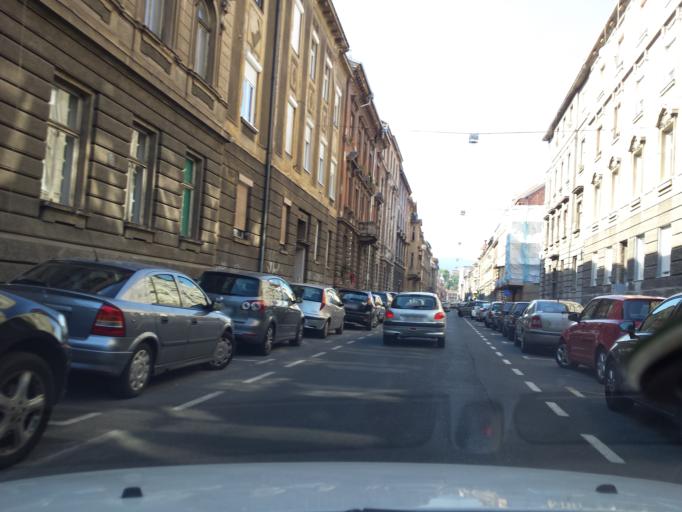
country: HR
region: Grad Zagreb
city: Zagreb - Centar
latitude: 45.8057
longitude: 15.9723
